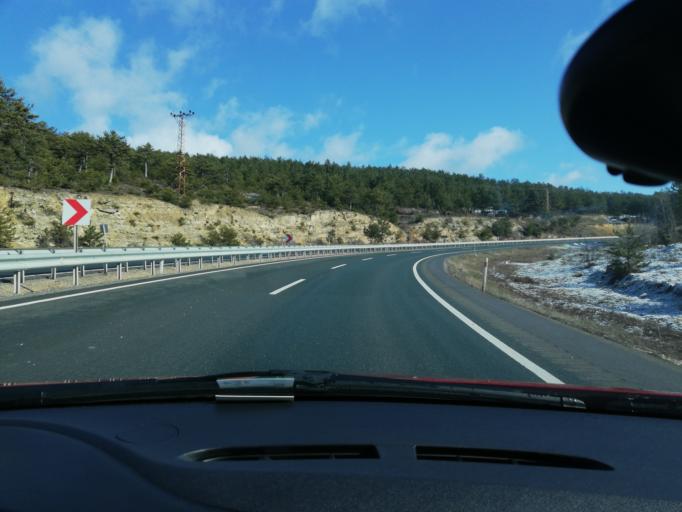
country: TR
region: Kastamonu
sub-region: Cide
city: Kastamonu
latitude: 41.3626
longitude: 33.7536
